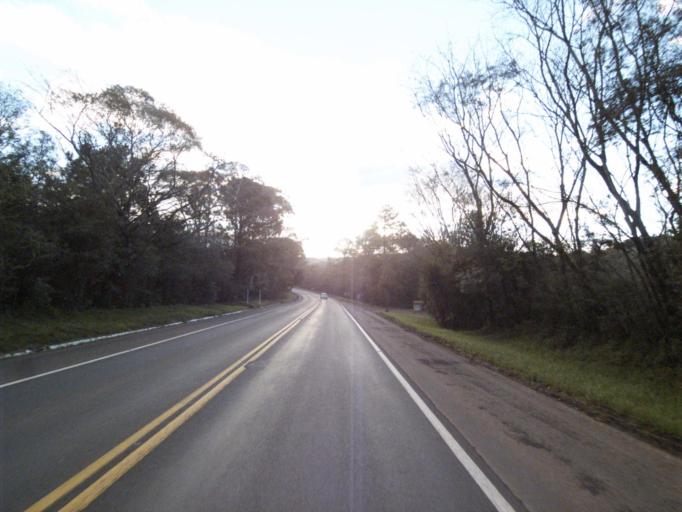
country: BR
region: Santa Catarina
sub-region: Joacaba
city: Joacaba
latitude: -27.2884
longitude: -51.4227
